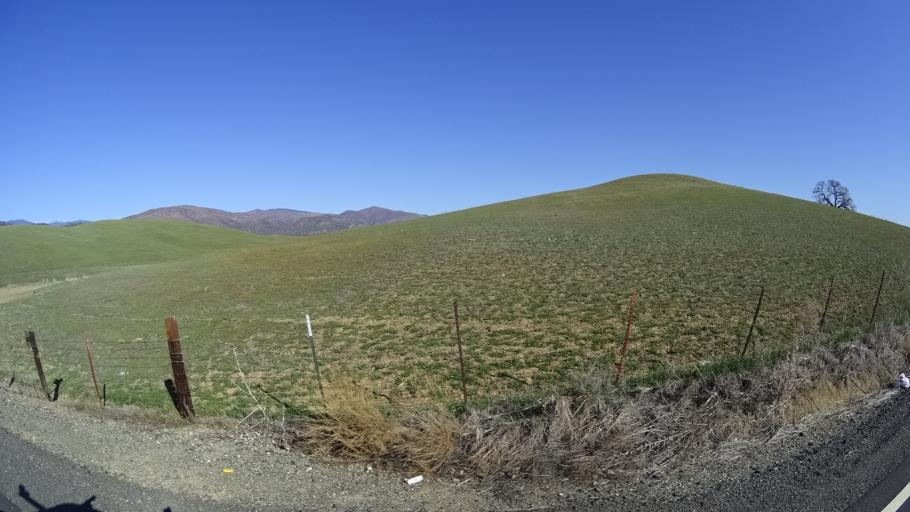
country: US
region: California
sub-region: Glenn County
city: Orland
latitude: 39.6599
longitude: -122.5432
